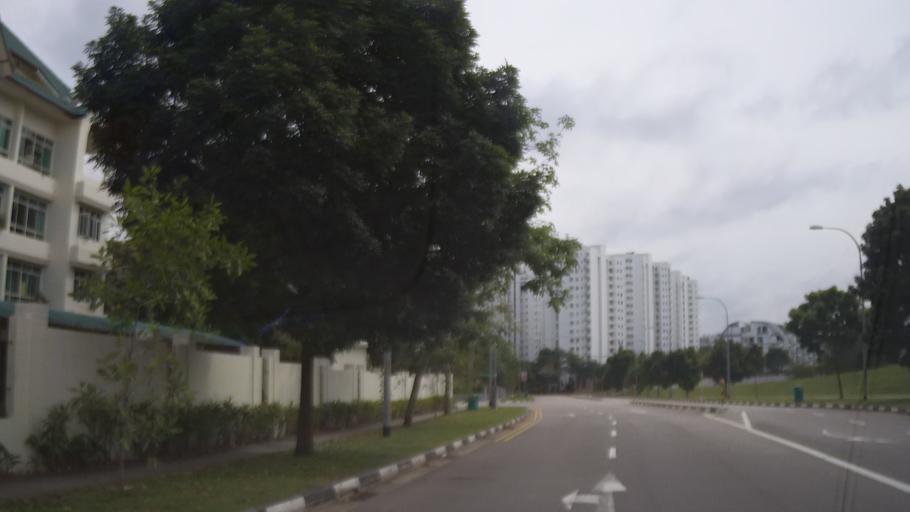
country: MY
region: Johor
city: Johor Bahru
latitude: 1.4289
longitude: 103.7830
